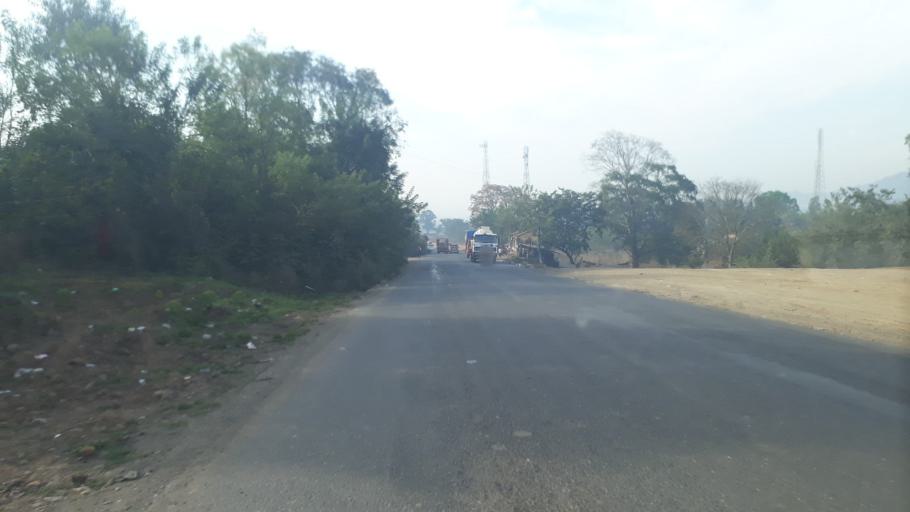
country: IN
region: Maharashtra
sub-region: Raigarh
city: Pen
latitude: 18.8578
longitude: 73.0998
